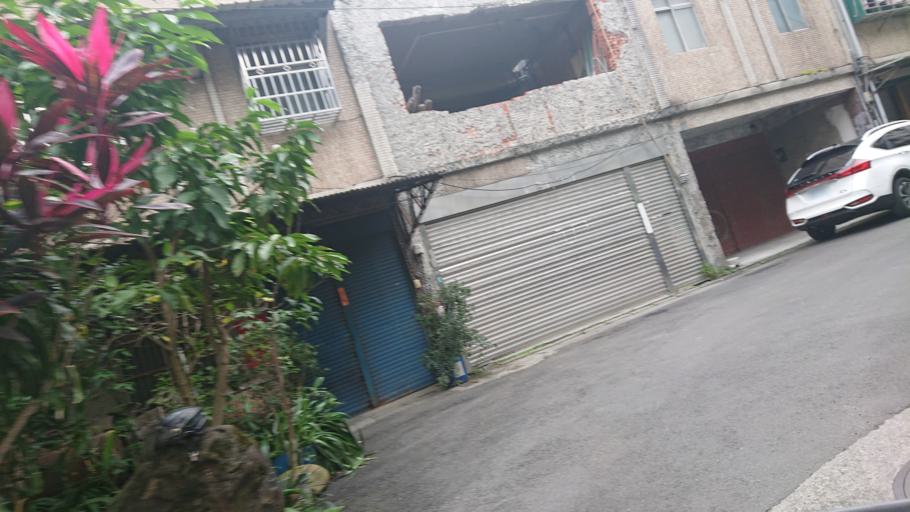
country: TW
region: Taiwan
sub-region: Taoyuan
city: Taoyuan
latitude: 24.9360
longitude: 121.3634
